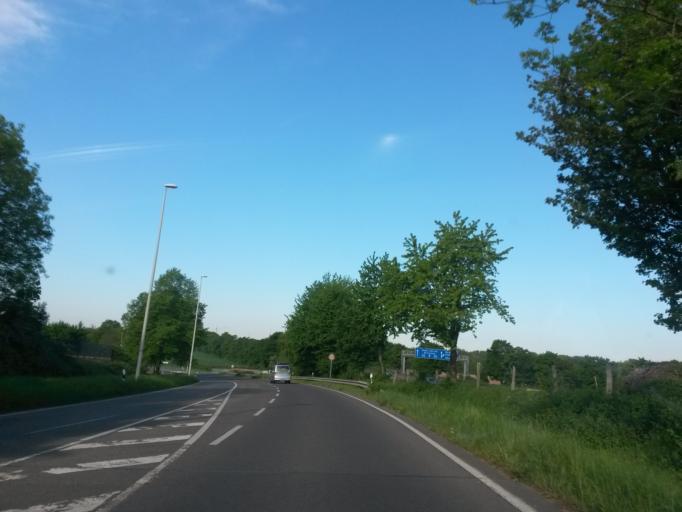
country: DE
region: North Rhine-Westphalia
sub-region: Regierungsbezirk Koln
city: Bonn
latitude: 50.7633
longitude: 7.1236
